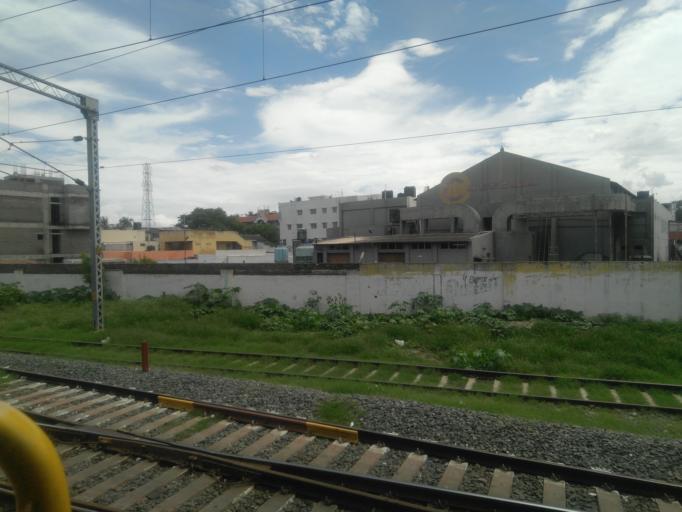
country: IN
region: Tamil Nadu
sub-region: Coimbatore
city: Coimbatore
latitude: 11.0161
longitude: 76.9562
